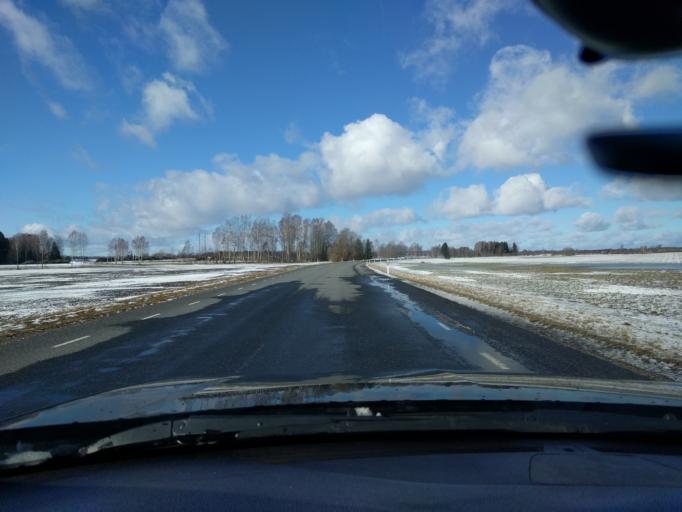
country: EE
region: Harju
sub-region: Anija vald
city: Kehra
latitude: 59.2425
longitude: 25.3602
